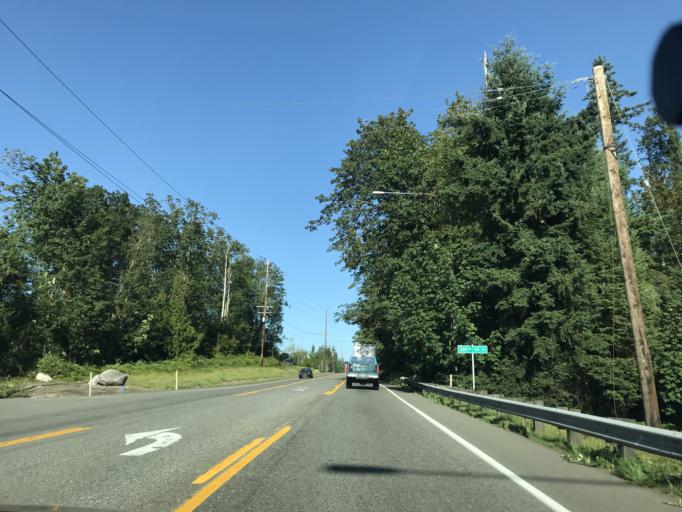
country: US
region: Washington
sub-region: King County
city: Maple Valley
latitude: 47.3579
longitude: -122.0634
